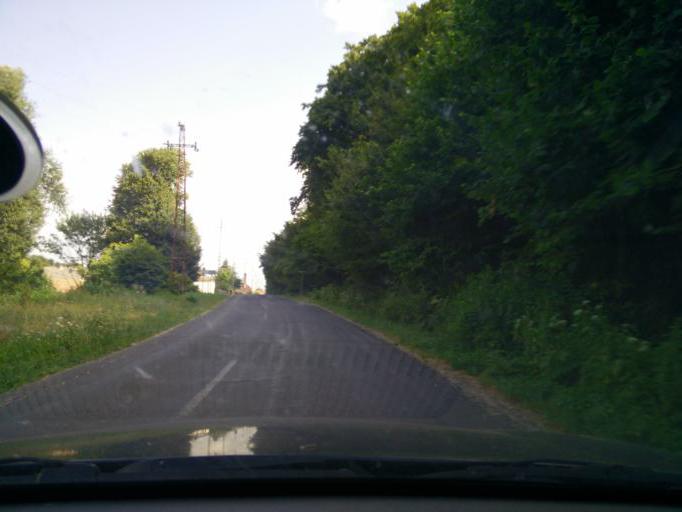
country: HU
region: Komarom-Esztergom
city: Tardos
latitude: 47.6677
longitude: 18.4441
